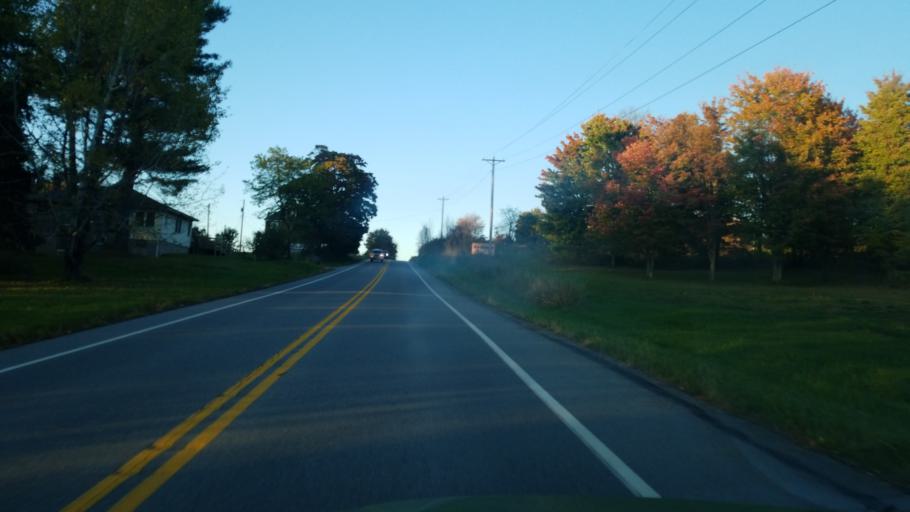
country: US
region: Pennsylvania
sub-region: Jefferson County
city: Reynoldsville
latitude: 41.0562
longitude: -78.9316
